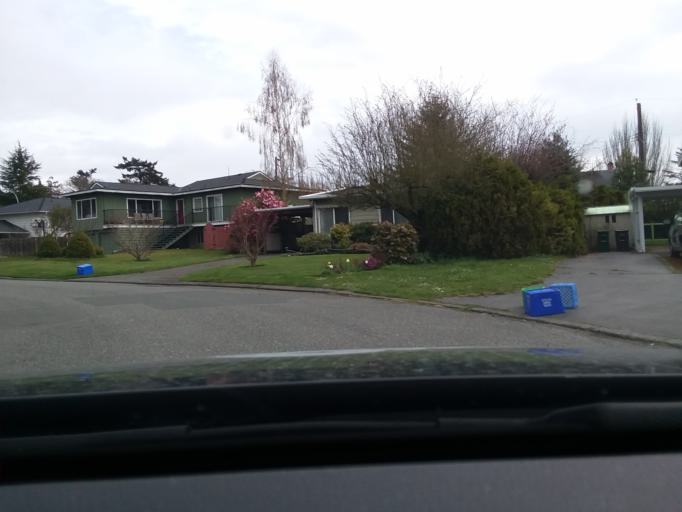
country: CA
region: British Columbia
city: Oak Bay
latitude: 48.4736
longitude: -123.3292
